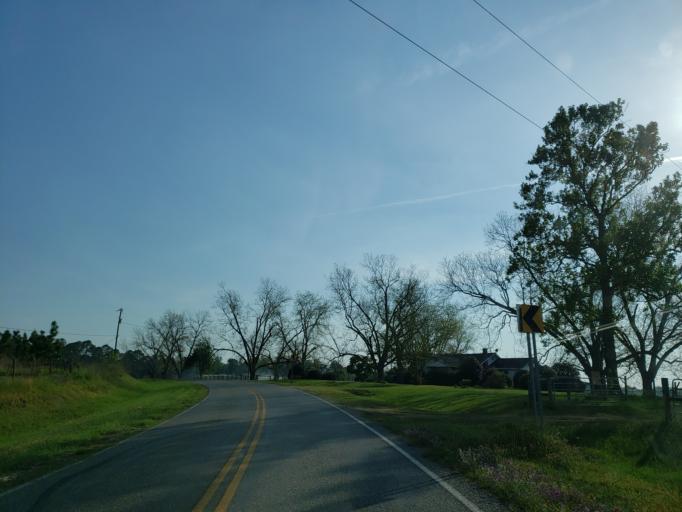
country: US
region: Georgia
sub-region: Tift County
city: Tifton
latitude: 31.5313
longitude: -83.5593
